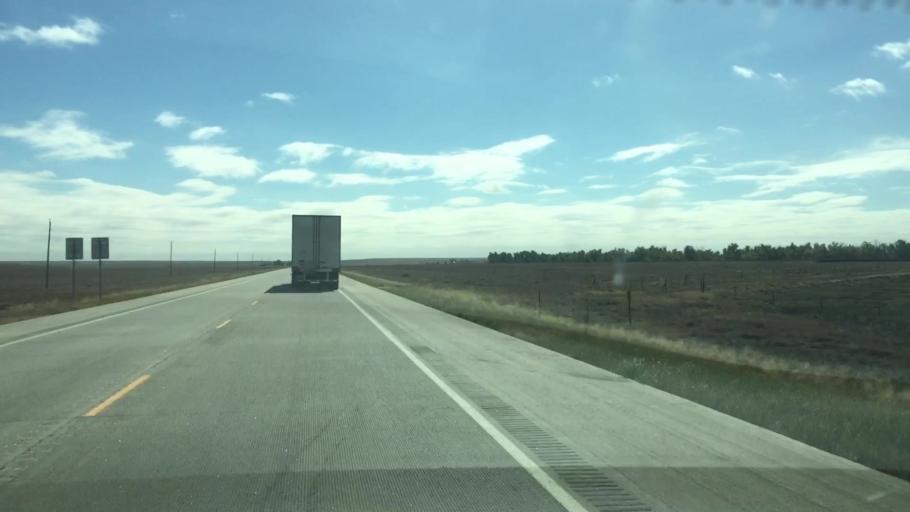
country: US
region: Colorado
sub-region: Lincoln County
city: Hugo
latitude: 39.0654
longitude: -103.3683
